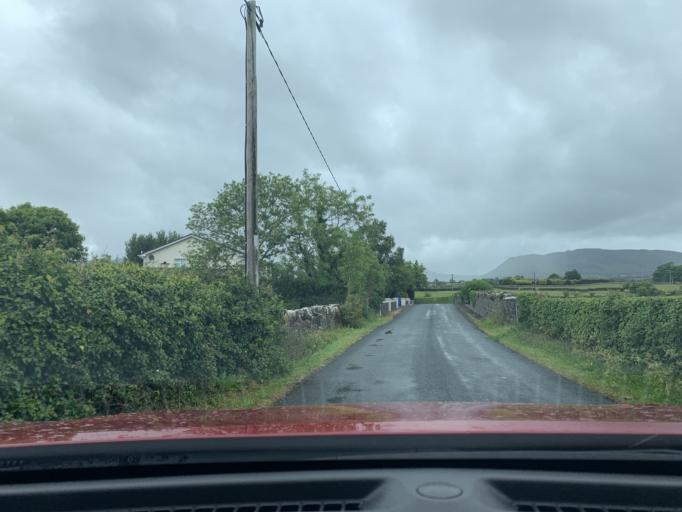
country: IE
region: Connaught
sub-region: Sligo
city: Sligo
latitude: 54.2947
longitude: -8.4628
